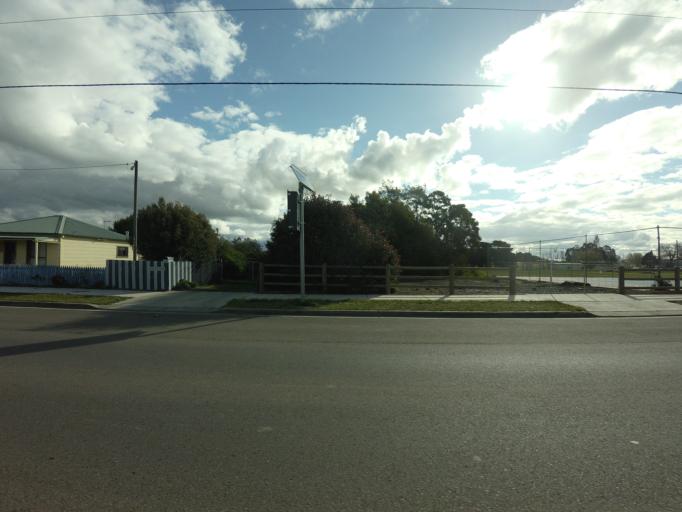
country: AU
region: Tasmania
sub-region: Northern Midlands
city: Longford
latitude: -41.6923
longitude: 147.0789
